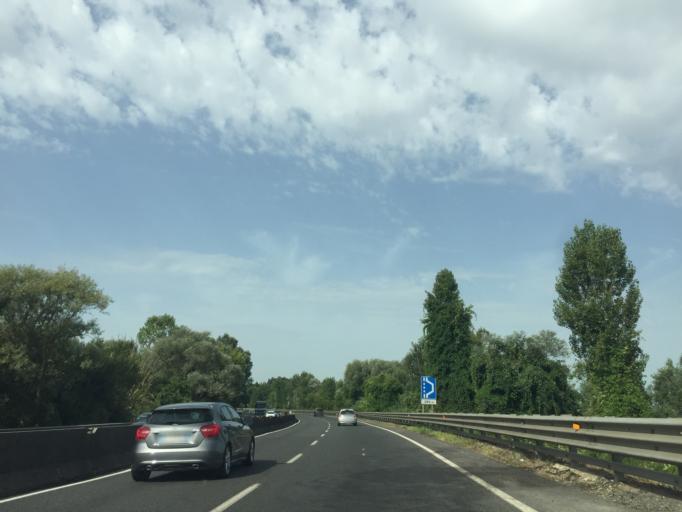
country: IT
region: Tuscany
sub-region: Province of Pisa
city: Marti
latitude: 43.6696
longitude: 10.7153
